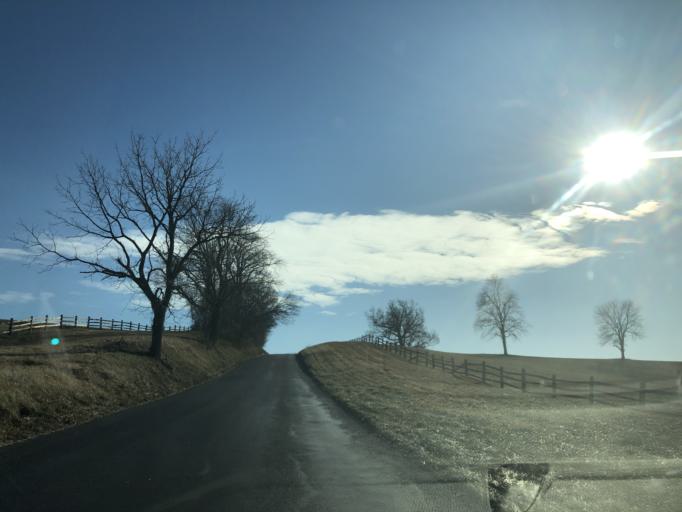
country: US
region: Pennsylvania
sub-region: Chester County
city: Upland
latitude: 39.8999
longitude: -75.7822
